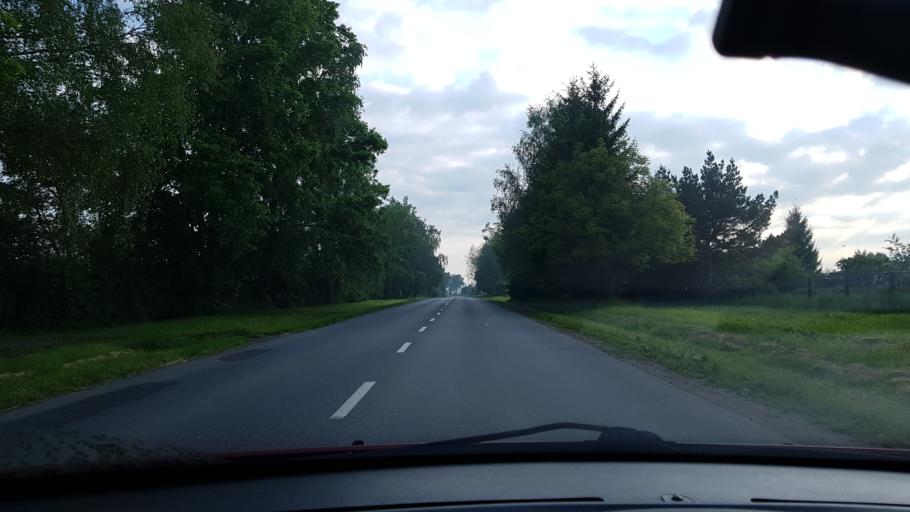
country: PL
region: Lower Silesian Voivodeship
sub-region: Powiat zabkowicki
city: Zabkowice Slaskie
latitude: 50.6050
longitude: 16.8215
